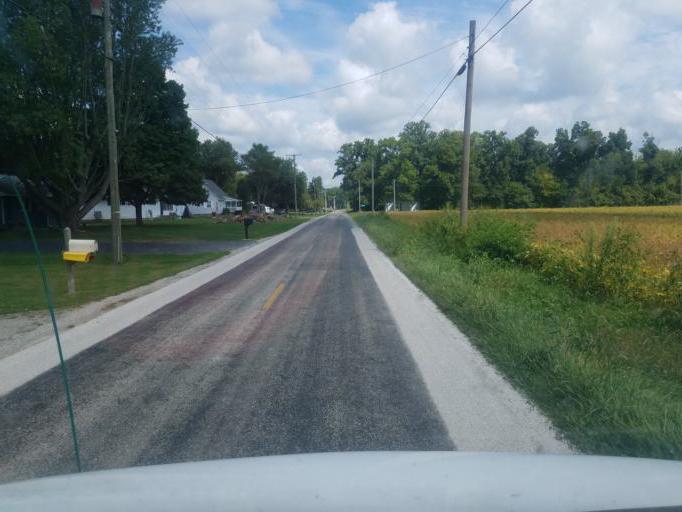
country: US
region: Ohio
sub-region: Marion County
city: Marion
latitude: 40.5116
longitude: -83.1313
